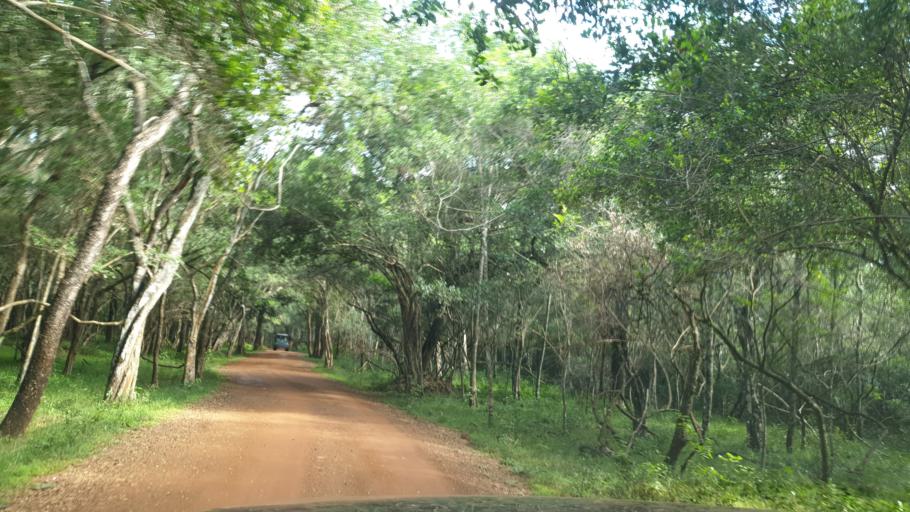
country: LK
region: North Central
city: Anuradhapura
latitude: 8.3815
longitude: 80.0635
